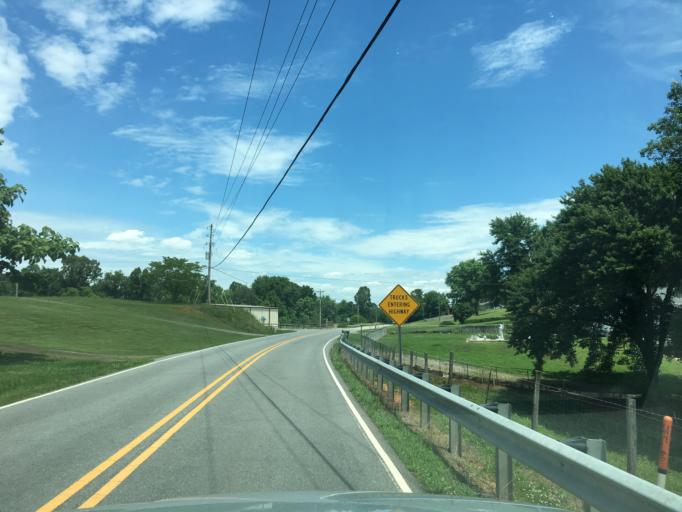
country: US
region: North Carolina
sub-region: Burke County
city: Glen Alpine
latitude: 35.6585
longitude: -81.7829
